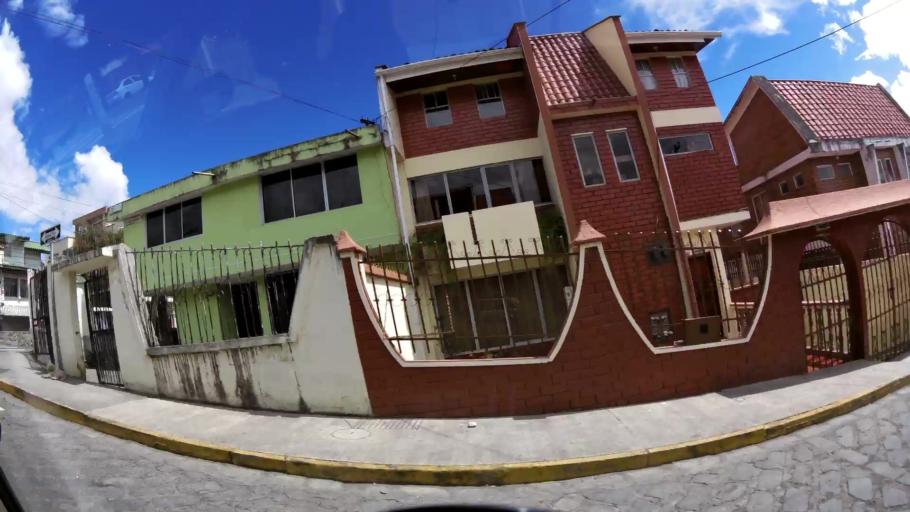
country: EC
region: Canar
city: Azogues
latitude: -2.7362
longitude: -78.8429
